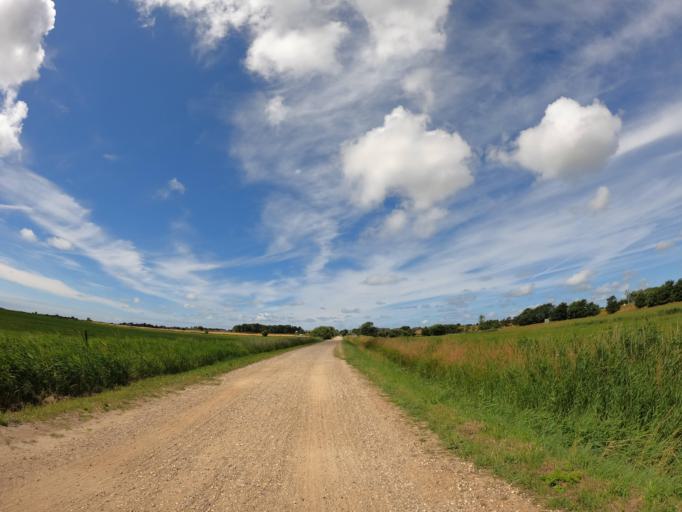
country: DE
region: Schleswig-Holstein
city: Tinnum
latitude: 54.8943
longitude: 8.3487
